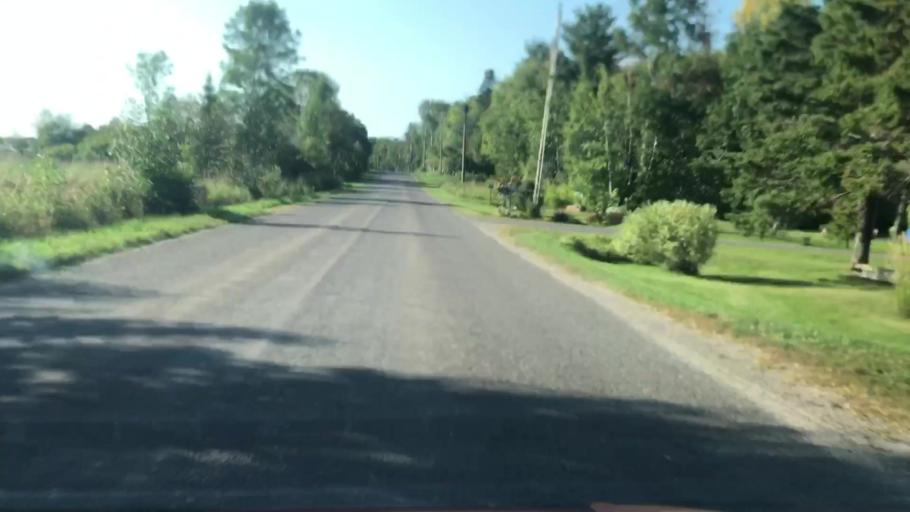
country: US
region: Michigan
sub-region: Chippewa County
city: Sault Ste. Marie
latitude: 46.2909
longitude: -84.0648
